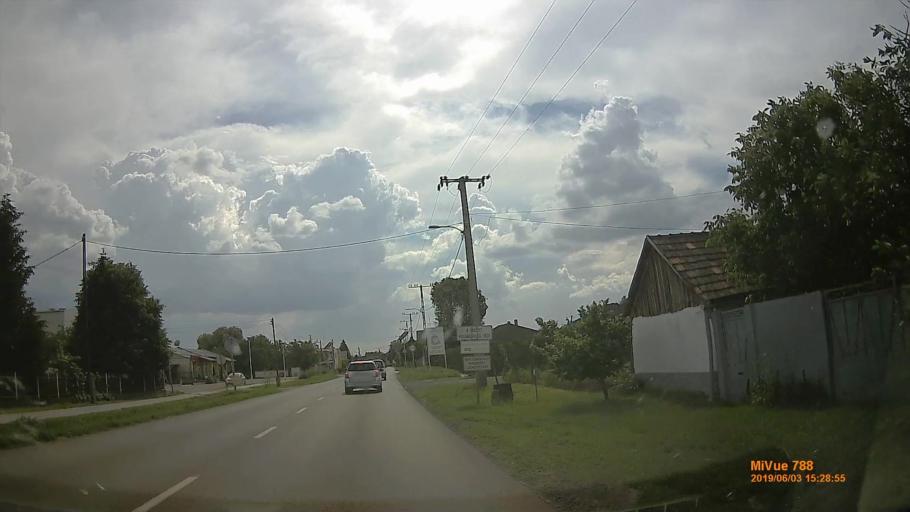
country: HU
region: Bacs-Kiskun
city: Soltvadkert
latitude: 46.5877
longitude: 19.3996
